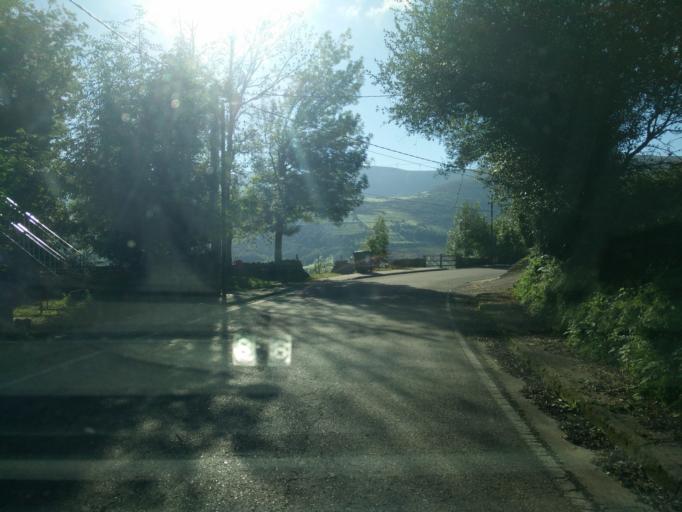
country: ES
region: Cantabria
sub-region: Provincia de Cantabria
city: San Pedro del Romeral
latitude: 43.1100
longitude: -3.8171
